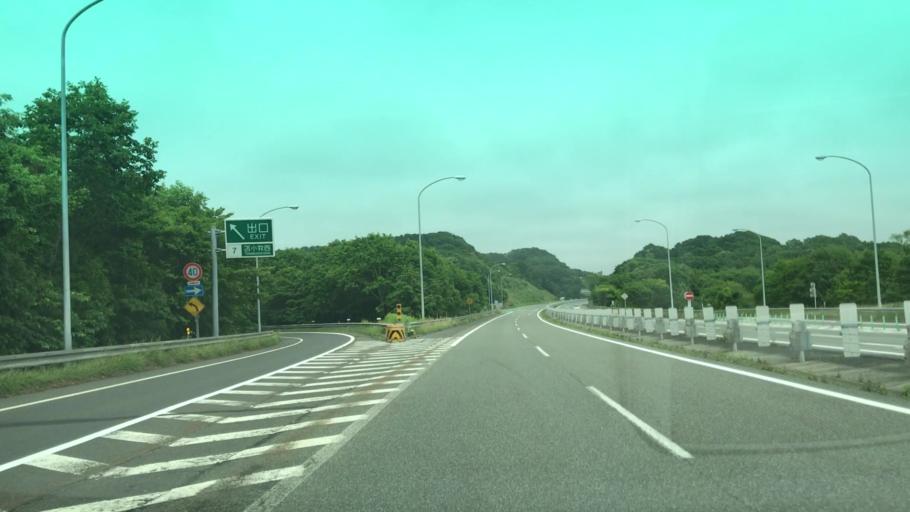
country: JP
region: Hokkaido
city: Tomakomai
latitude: 42.6316
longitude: 141.4880
